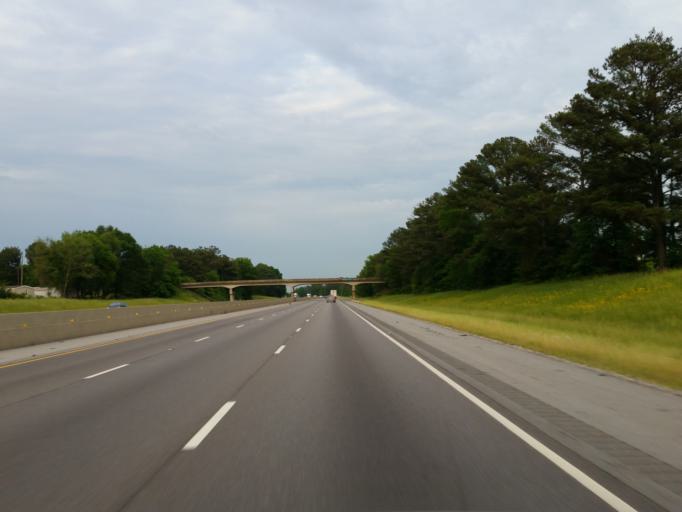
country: US
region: Alabama
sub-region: Calhoun County
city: Oxford
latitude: 33.5851
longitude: -85.8922
